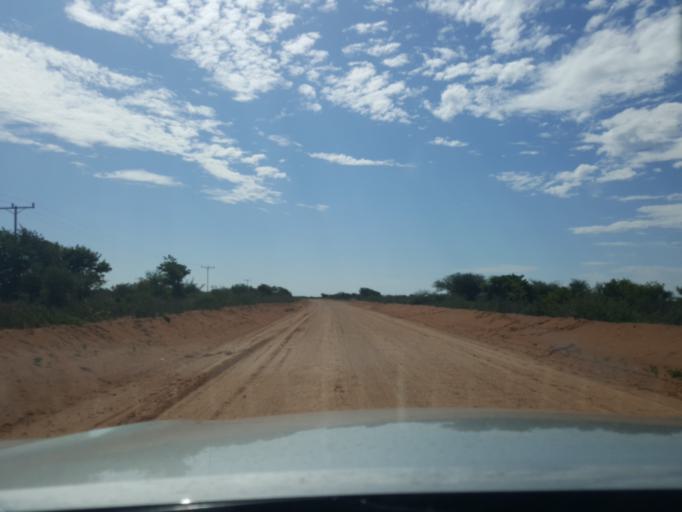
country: BW
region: Kweneng
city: Khudumelapye
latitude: -23.8466
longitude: 24.8627
